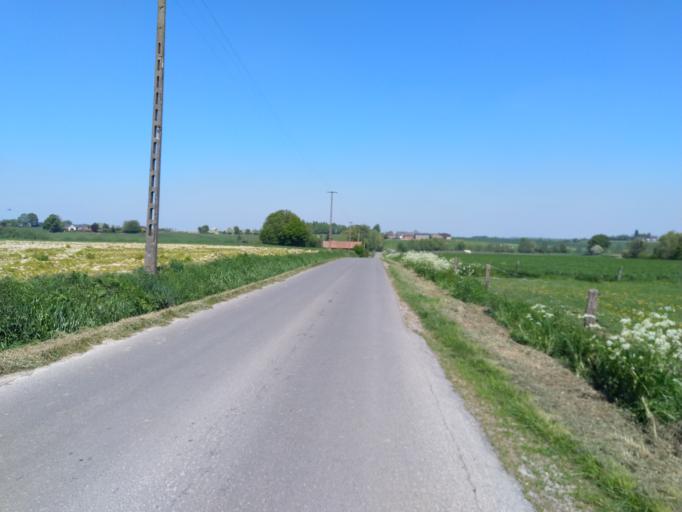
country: BE
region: Wallonia
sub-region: Province du Hainaut
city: Enghien
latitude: 50.6417
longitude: 4.0251
